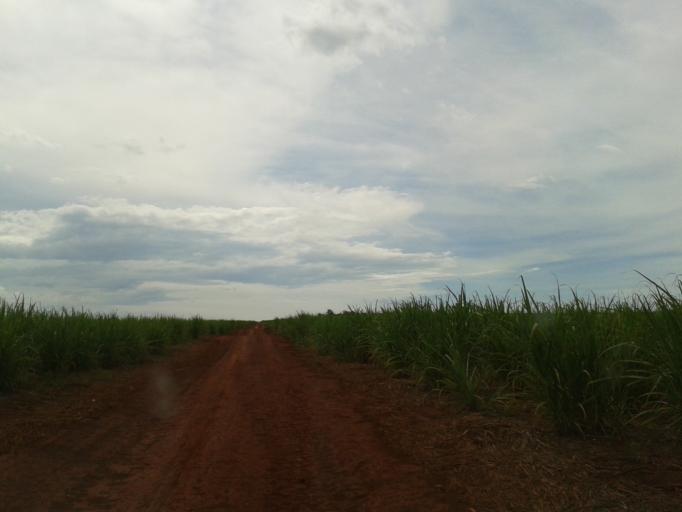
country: BR
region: Minas Gerais
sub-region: Centralina
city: Centralina
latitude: -18.6639
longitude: -49.2414
